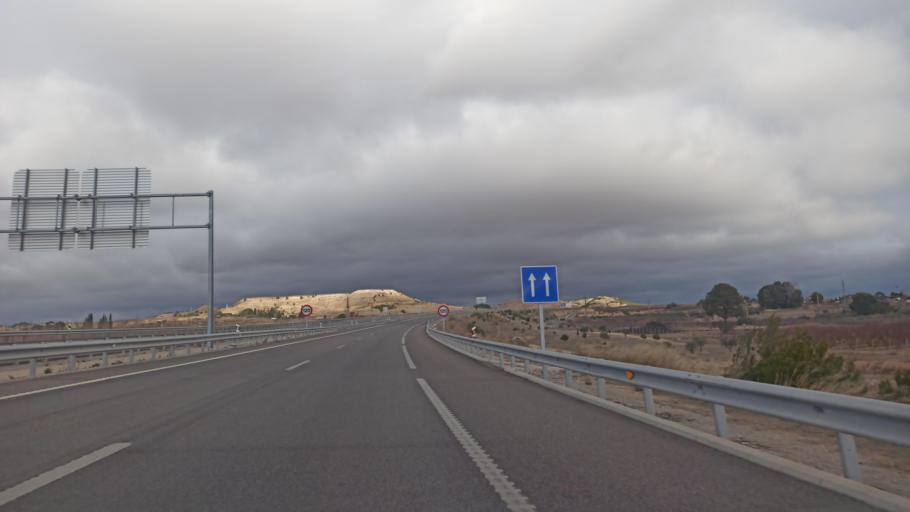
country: ES
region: Catalonia
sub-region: Provincia de Lleida
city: Alpicat
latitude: 41.6600
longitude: 0.5823
